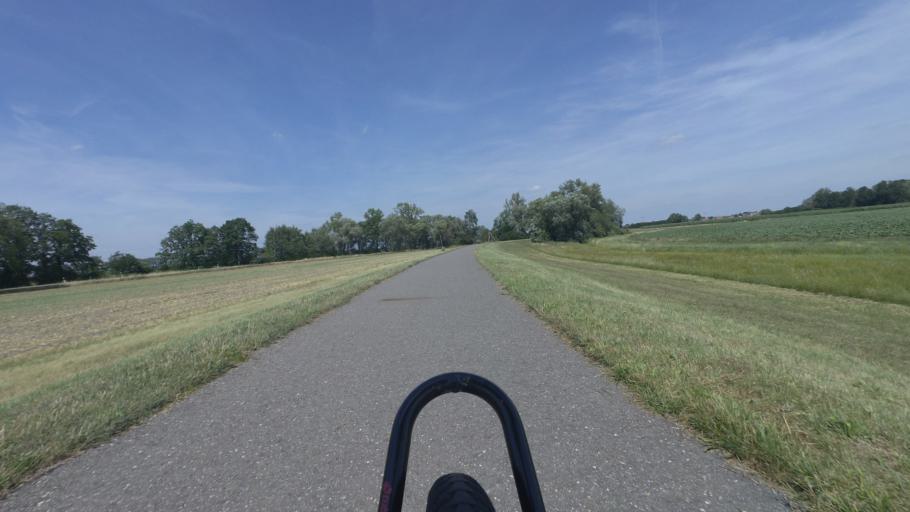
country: DE
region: Saxony-Anhalt
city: Kamern
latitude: 52.7693
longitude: 12.1912
